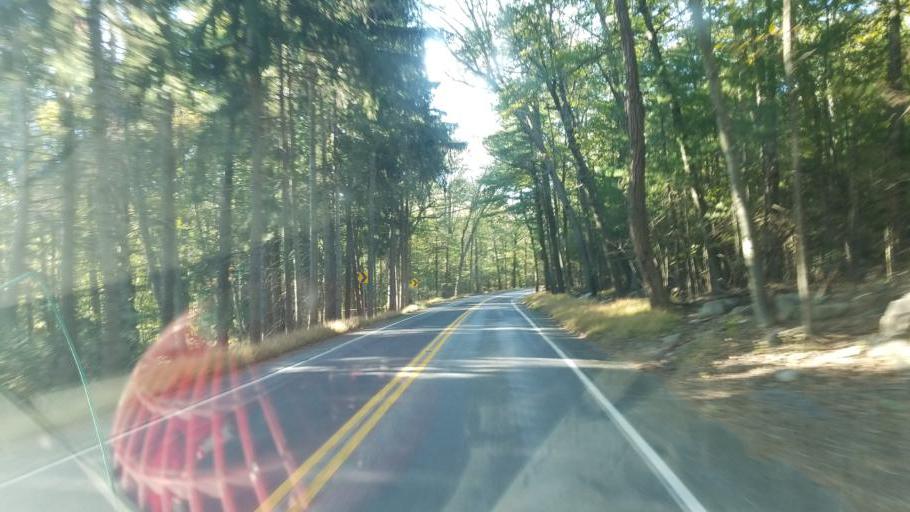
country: US
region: Pennsylvania
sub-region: Franklin County
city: Mont Alto
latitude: 39.8590
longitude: -77.5022
